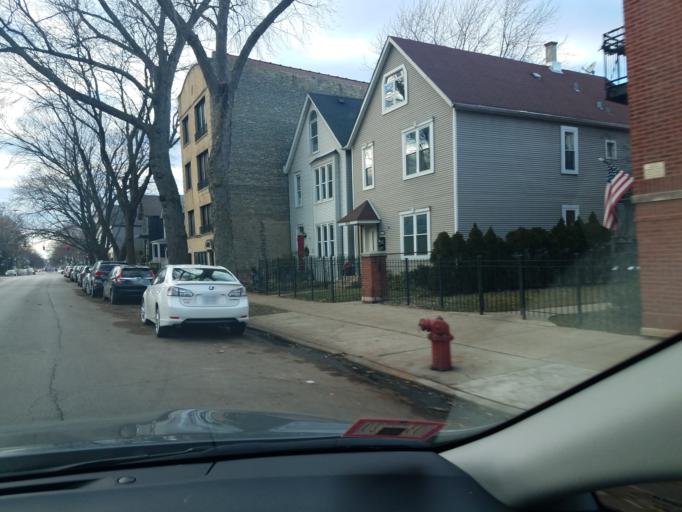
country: US
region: Illinois
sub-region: Cook County
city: Lincolnwood
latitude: 41.9433
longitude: -87.6771
